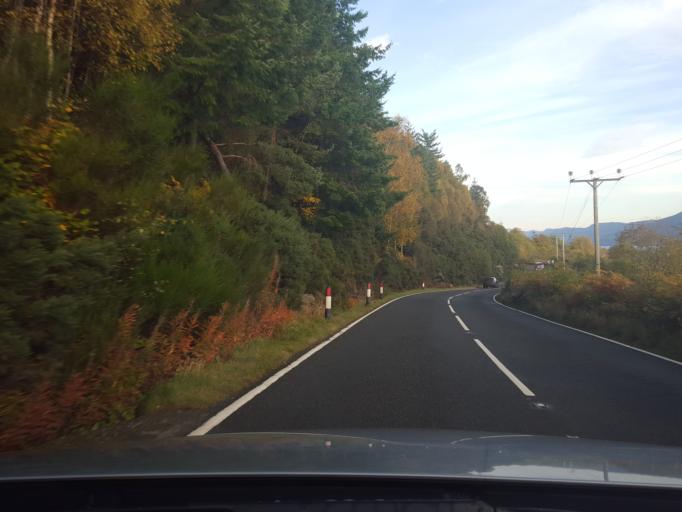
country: GB
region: Scotland
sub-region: Highland
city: Beauly
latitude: 57.2190
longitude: -4.5830
